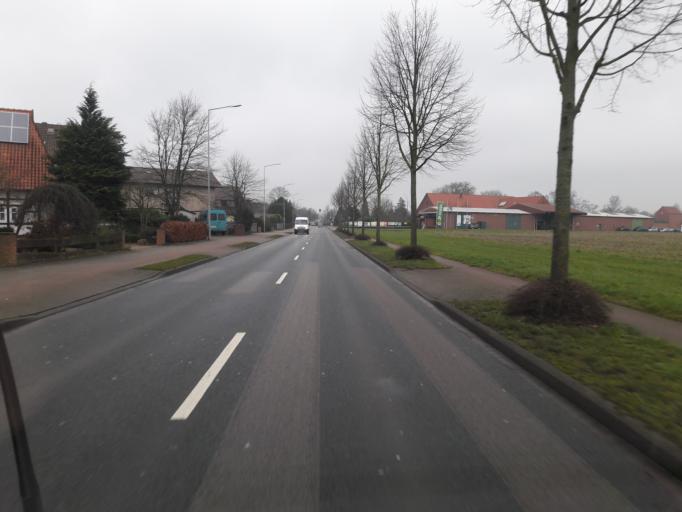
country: DE
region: North Rhine-Westphalia
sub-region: Regierungsbezirk Detmold
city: Minden
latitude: 52.3059
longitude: 8.8499
